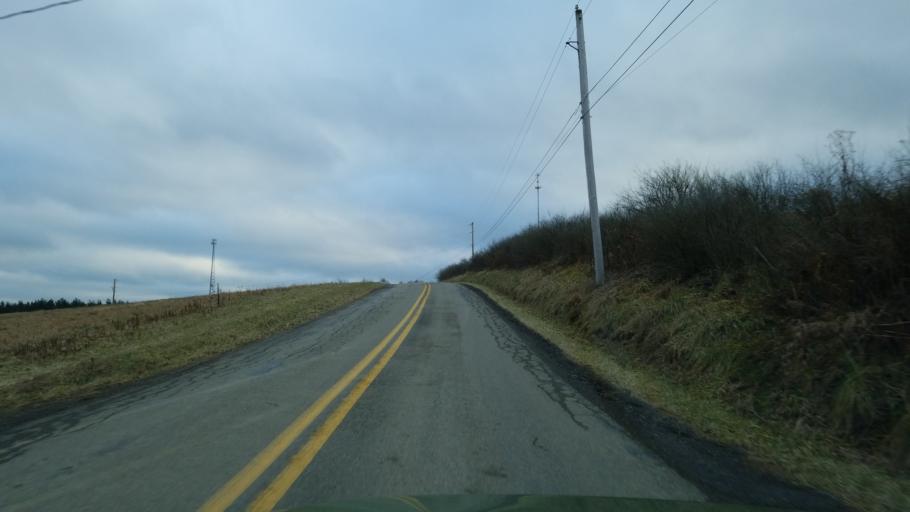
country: US
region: Pennsylvania
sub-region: Jefferson County
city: Falls Creek
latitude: 41.1720
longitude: -78.8127
